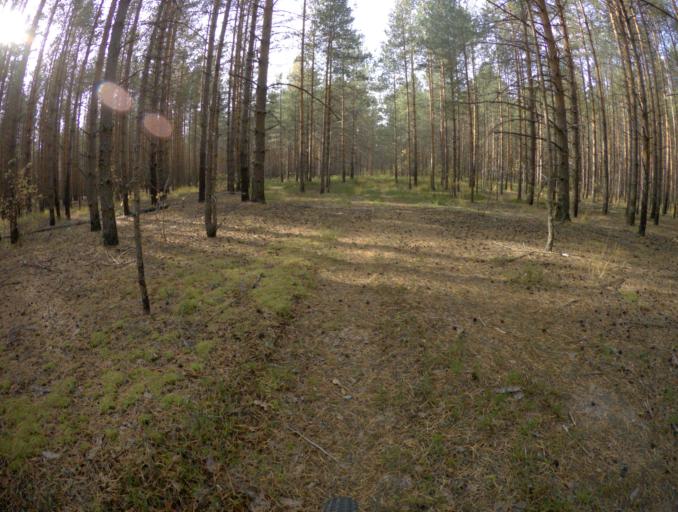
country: RU
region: Vladimir
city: Sobinka
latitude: 55.9272
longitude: 40.0490
